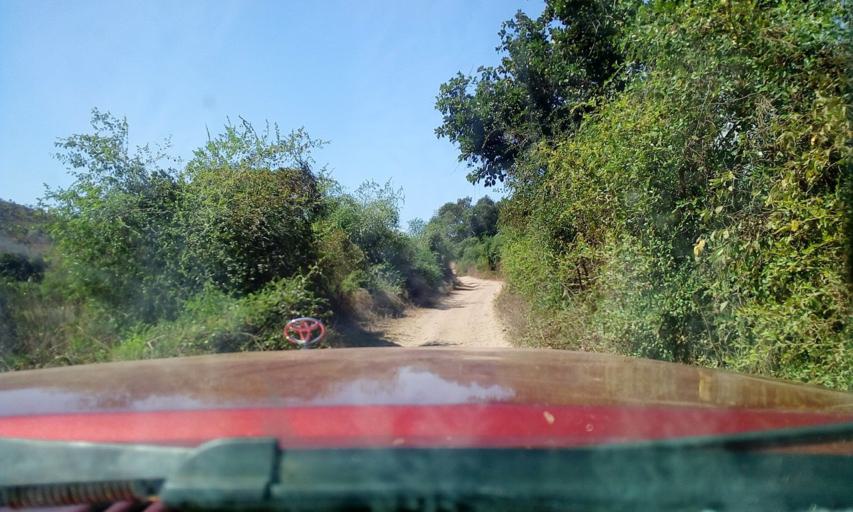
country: MG
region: Boeny
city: Sitampiky
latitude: -16.1262
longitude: 45.4752
